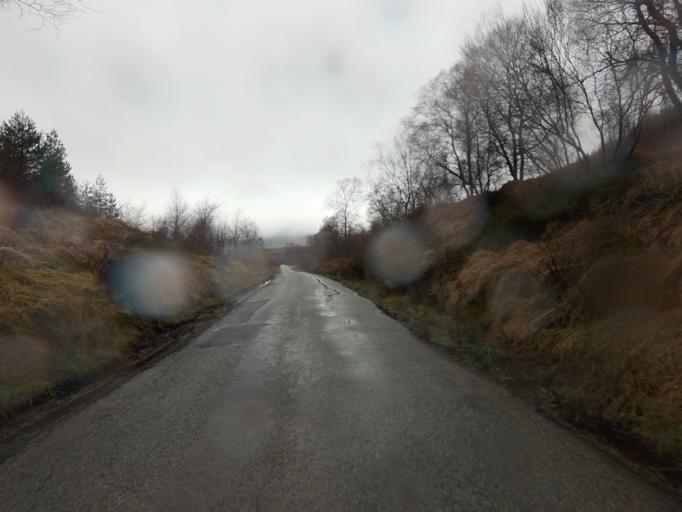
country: GB
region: Scotland
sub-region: West Dunbartonshire
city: Balloch
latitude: 56.2427
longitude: -4.5715
